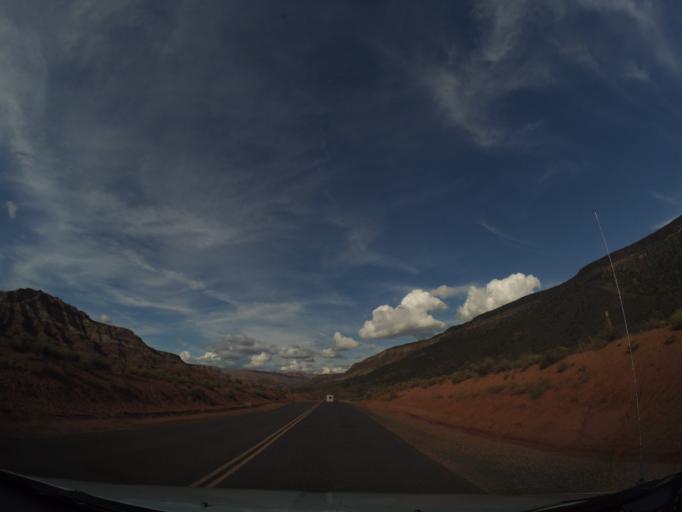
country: US
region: Utah
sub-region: Washington County
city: LaVerkin
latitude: 37.2181
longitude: -113.1661
